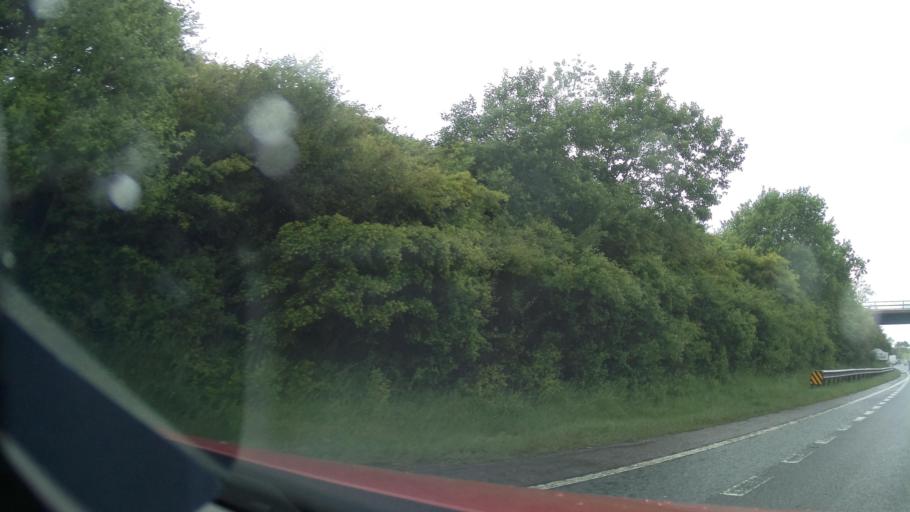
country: GB
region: England
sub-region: Sunderland
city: Ryhope
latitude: 54.8478
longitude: -1.3825
